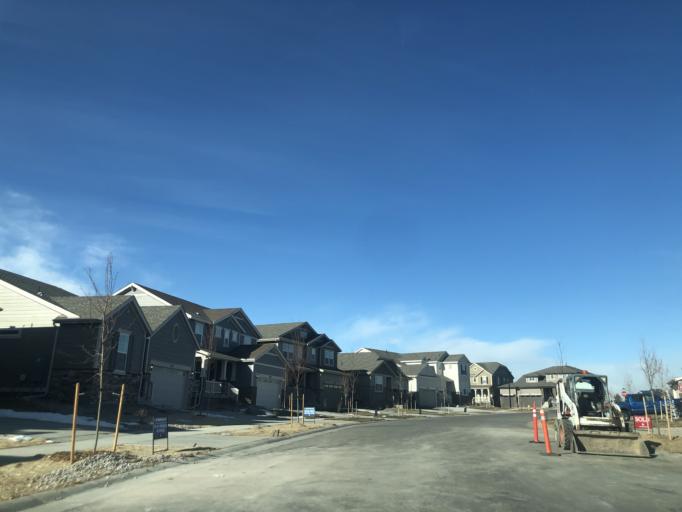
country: US
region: Colorado
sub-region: Douglas County
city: Stonegate
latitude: 39.5574
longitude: -104.8046
